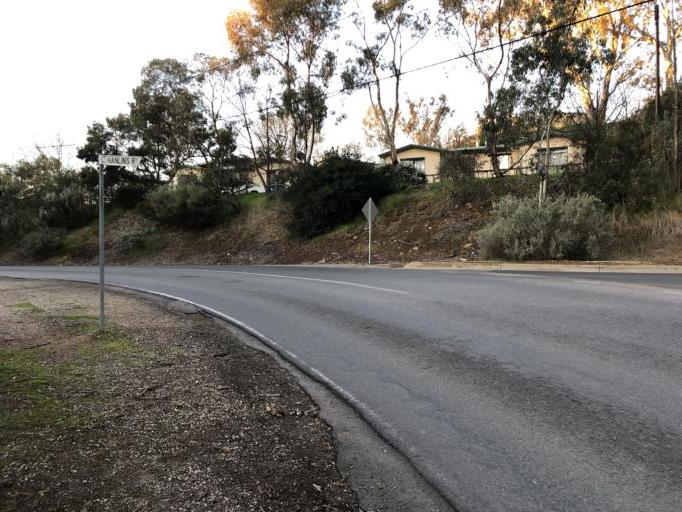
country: AU
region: South Australia
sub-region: Clare and Gilbert Valleys
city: Clare
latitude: -33.8424
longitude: 138.6131
